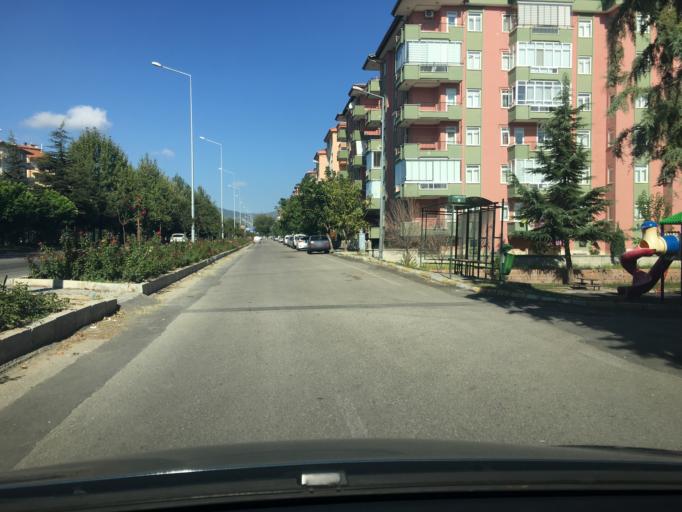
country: TR
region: Isparta
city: Isparta
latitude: 37.7892
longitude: 30.5524
